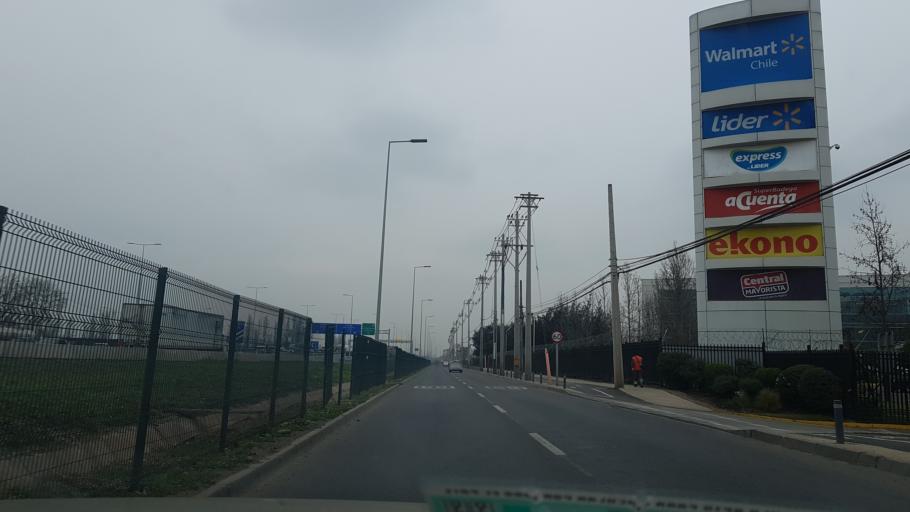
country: CL
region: Santiago Metropolitan
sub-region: Provincia de Santiago
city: Lo Prado
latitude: -33.3621
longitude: -70.7016
